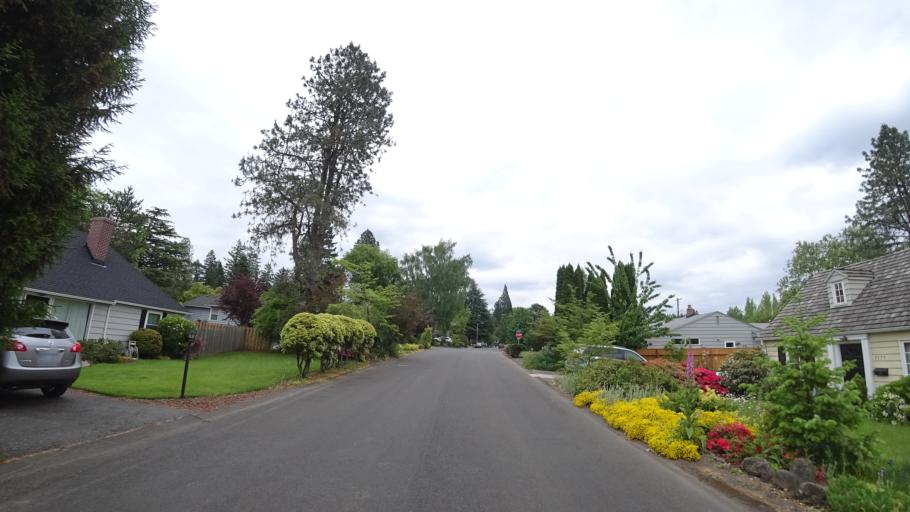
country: US
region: Oregon
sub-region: Washington County
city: Raleigh Hills
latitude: 45.4829
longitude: -122.7763
